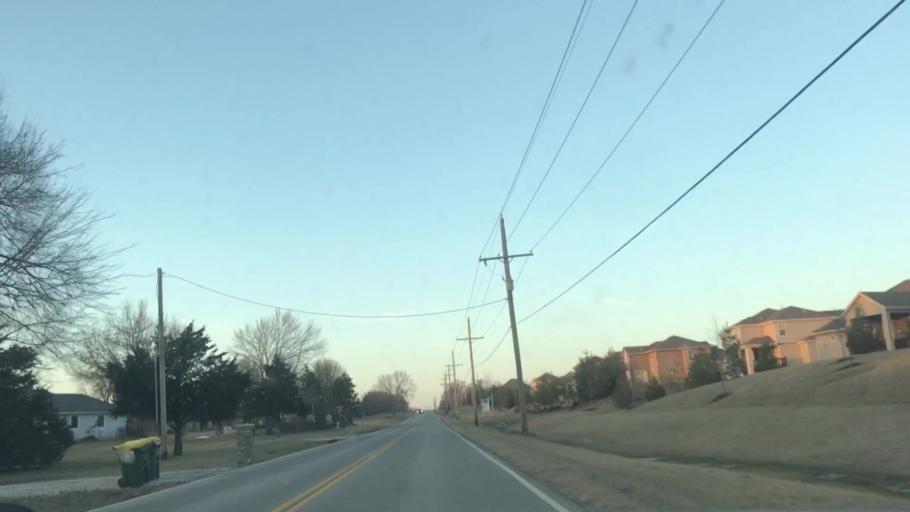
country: US
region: Kansas
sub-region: Johnson County
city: Olathe
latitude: 38.8303
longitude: -94.7052
